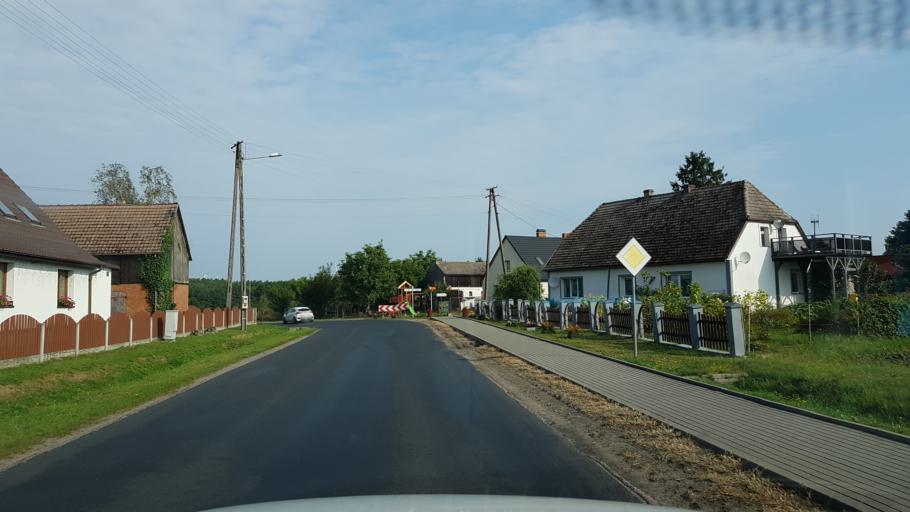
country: PL
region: West Pomeranian Voivodeship
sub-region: Powiat slawienski
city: Slawno
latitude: 54.4375
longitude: 16.6138
